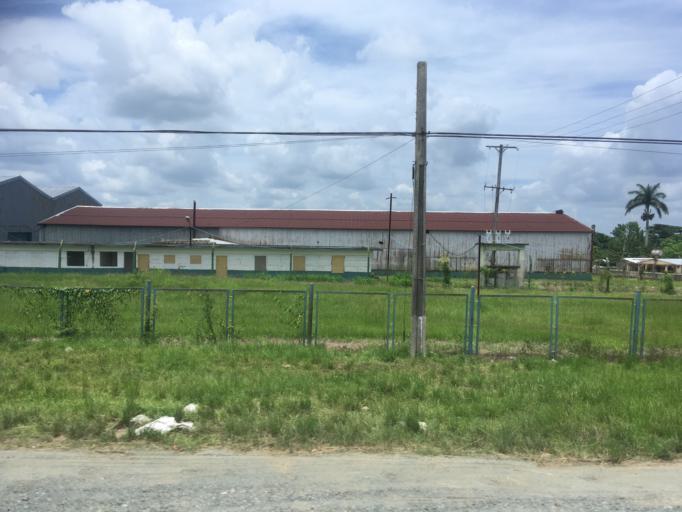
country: CU
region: Villa Clara
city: Esperanza
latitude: 22.4140
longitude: -80.0408
